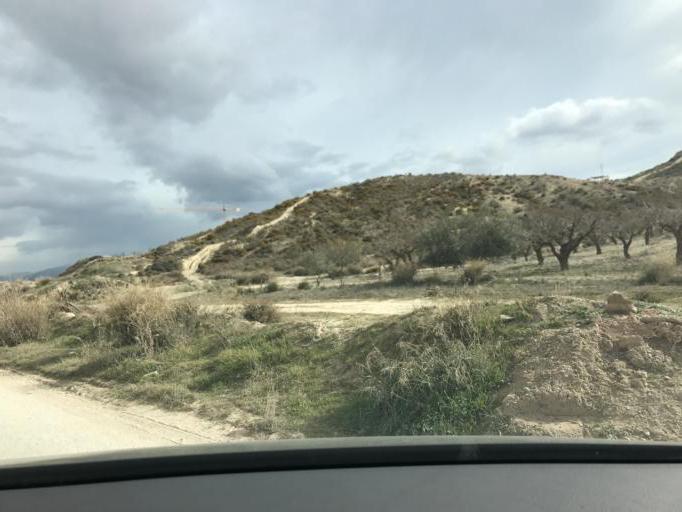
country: ES
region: Andalusia
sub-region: Provincia de Granada
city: Alhendin
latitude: 37.1039
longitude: -3.6675
